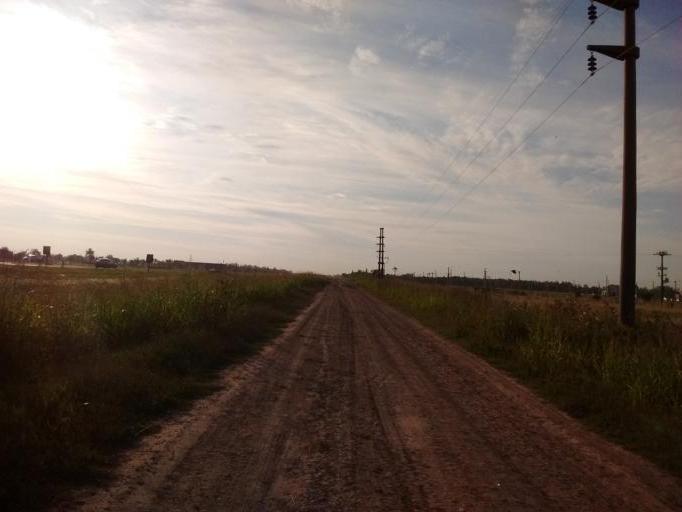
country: AR
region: Santa Fe
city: Roldan
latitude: -32.9304
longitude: -60.8706
